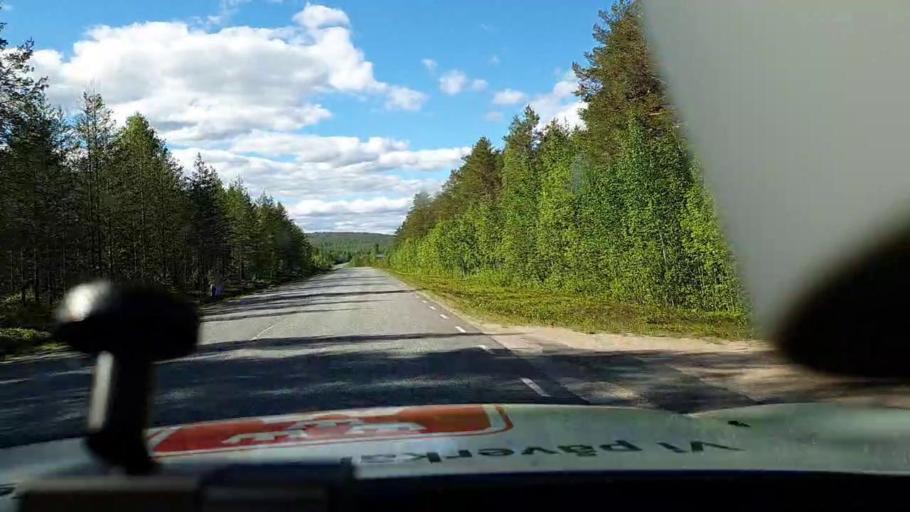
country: FI
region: Lapland
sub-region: Torniolaakso
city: Ylitornio
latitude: 66.2968
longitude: 23.6366
